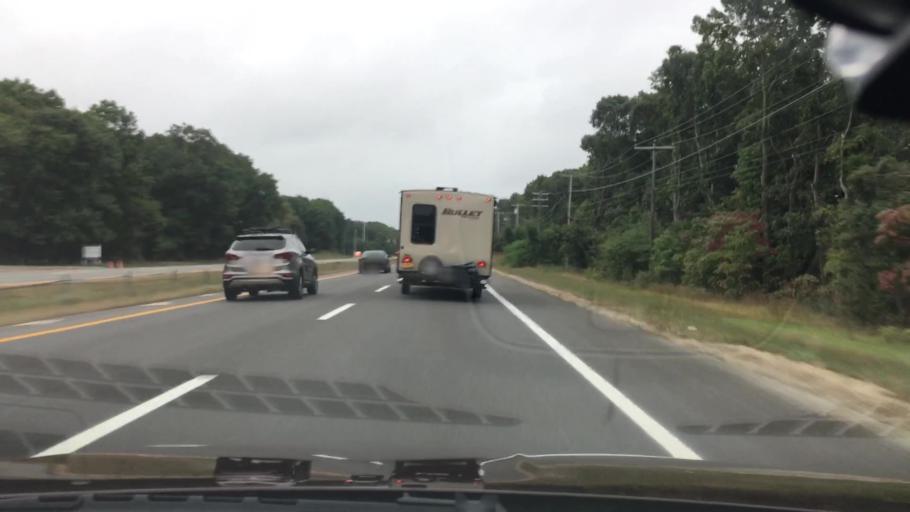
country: US
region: New York
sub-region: Suffolk County
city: Setauket-East Setauket
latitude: 40.8956
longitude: -73.1131
